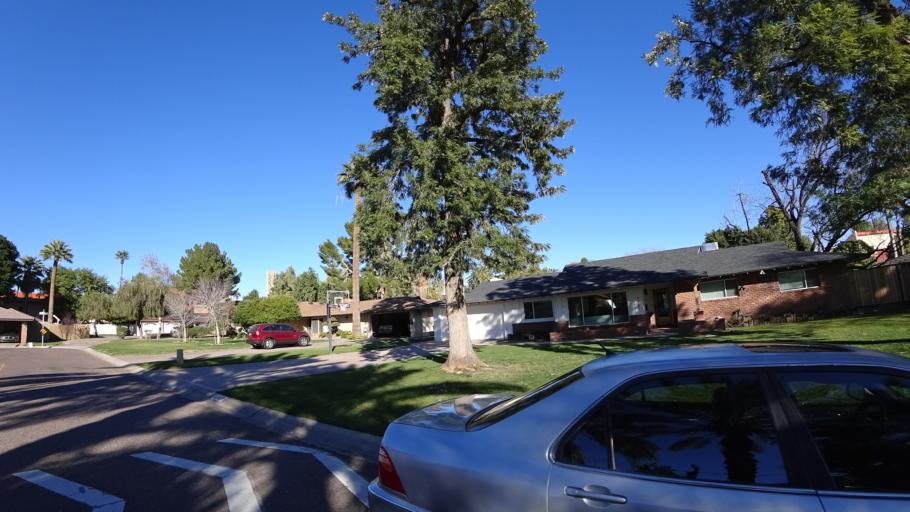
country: US
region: Arizona
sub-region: Maricopa County
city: Phoenix
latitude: 33.5365
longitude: -112.0758
